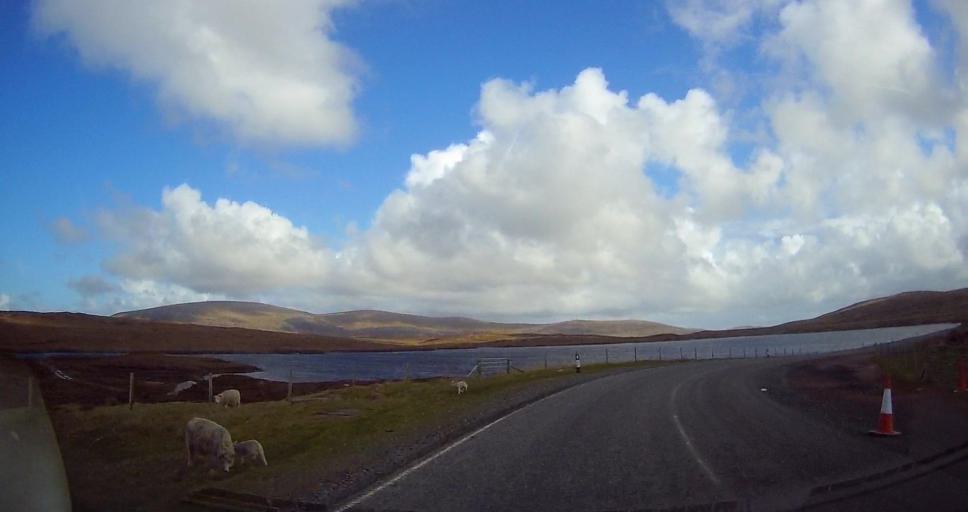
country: GB
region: Scotland
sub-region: Shetland Islands
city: Lerwick
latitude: 60.4849
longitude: -1.4033
